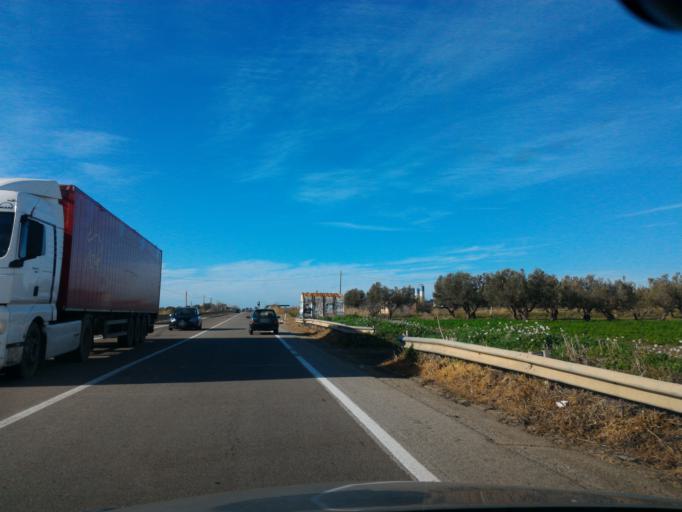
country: IT
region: Calabria
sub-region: Provincia di Crotone
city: Isola di Capo Rizzuto
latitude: 38.9377
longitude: 17.0607
